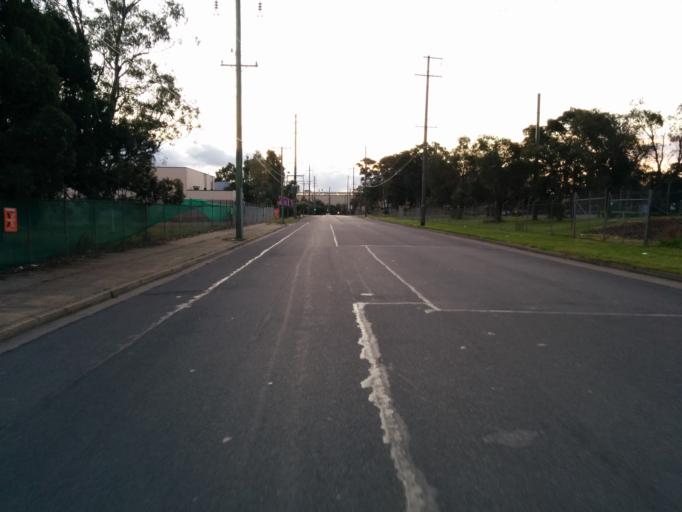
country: AU
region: New South Wales
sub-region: Holroyd
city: Guildford West
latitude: -33.8583
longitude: 150.9618
